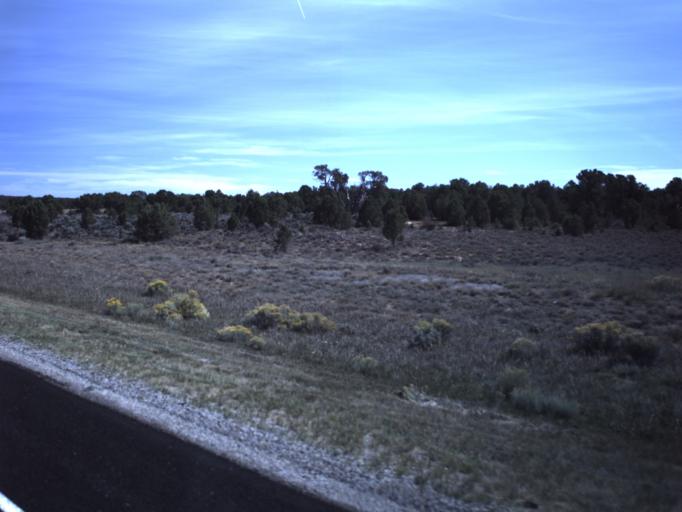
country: US
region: Colorado
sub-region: Dolores County
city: Dove Creek
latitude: 37.8376
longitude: -109.1157
